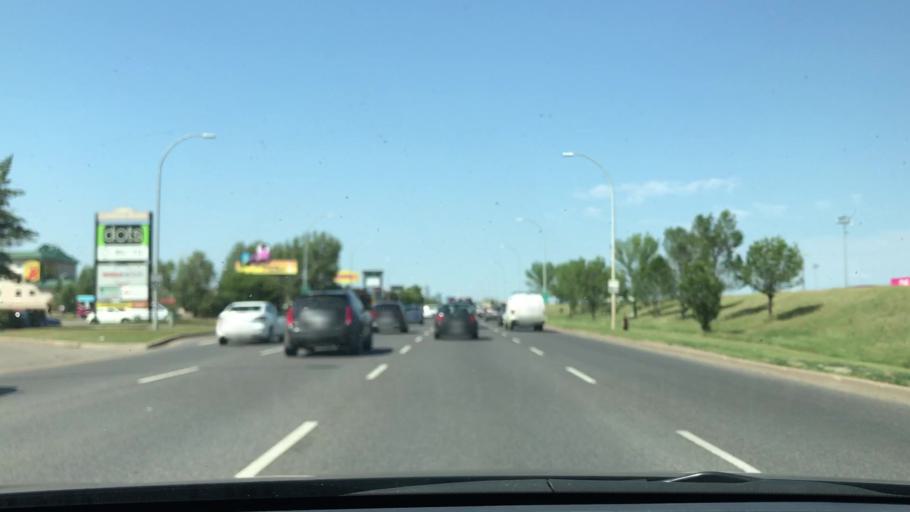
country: CA
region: Alberta
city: Edmonton
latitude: 53.4681
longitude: -113.4921
